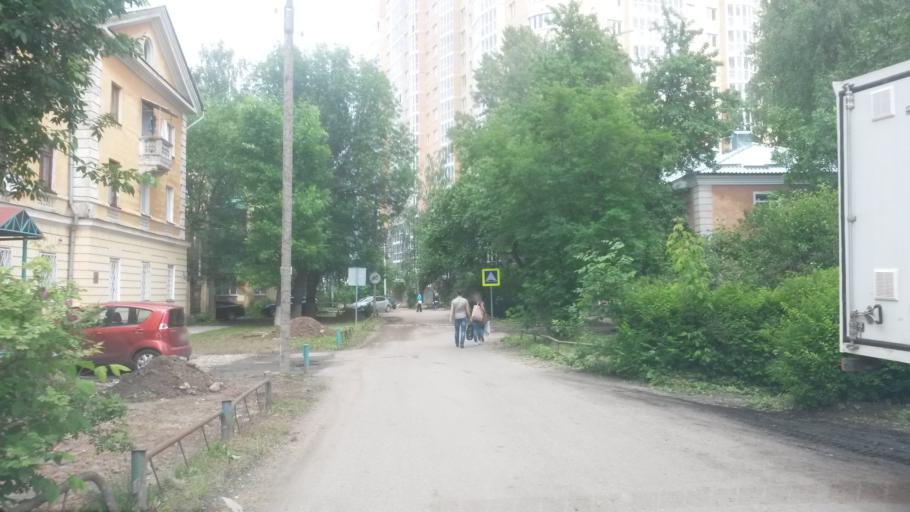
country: RU
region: Jaroslavl
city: Yaroslavl
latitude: 57.6405
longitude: 39.8691
